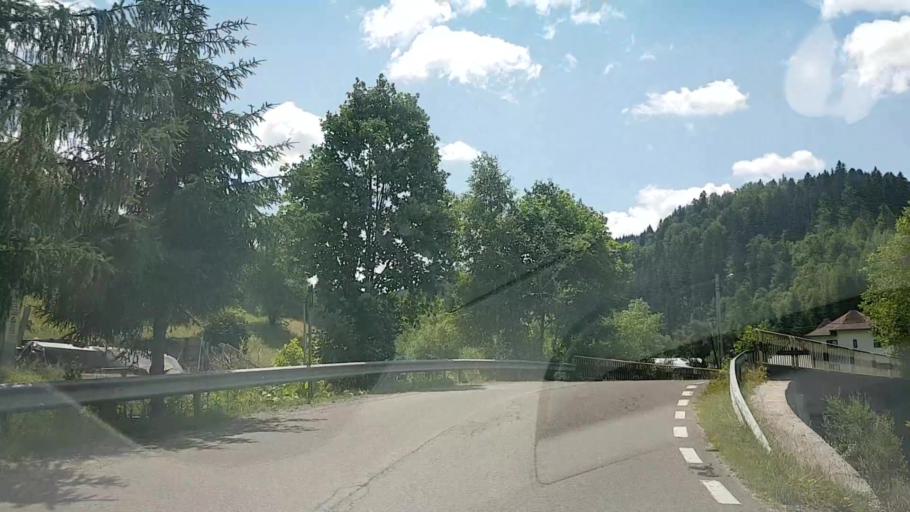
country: RO
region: Suceava
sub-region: Comuna Sadova
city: Sadova
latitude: 47.4835
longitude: 25.4919
